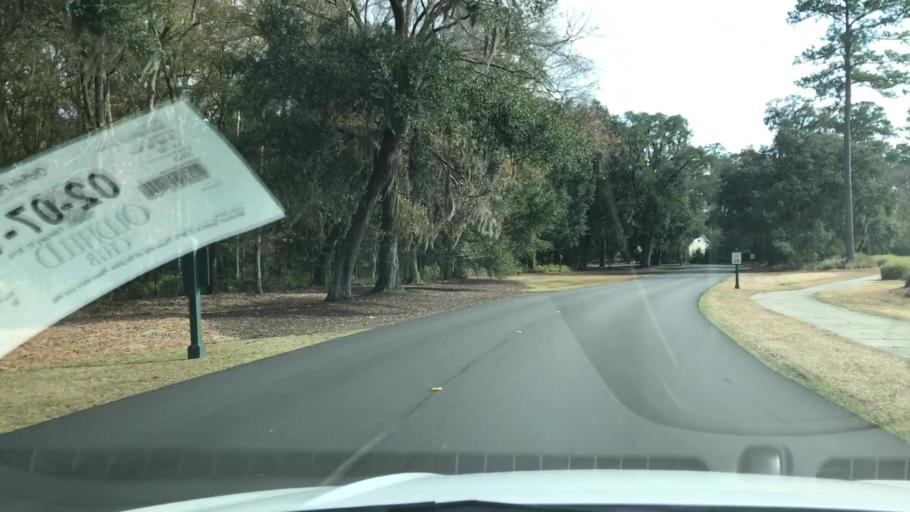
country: US
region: South Carolina
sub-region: Beaufort County
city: Bluffton
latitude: 32.3432
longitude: -80.9185
